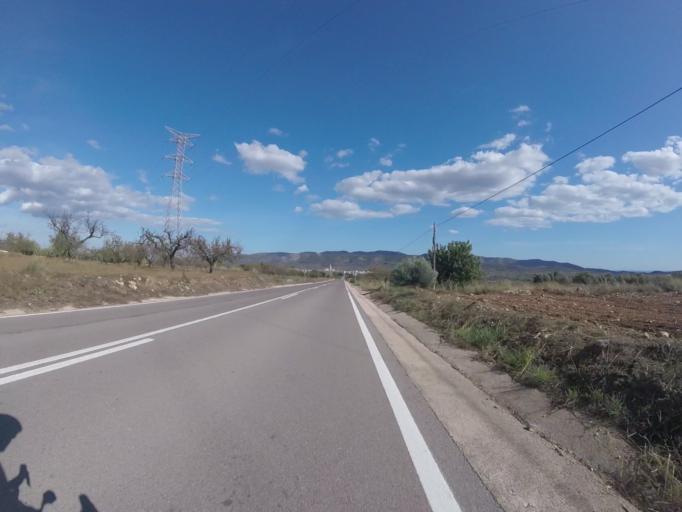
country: ES
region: Valencia
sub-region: Provincia de Castello
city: Alcala de Xivert
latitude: 40.3023
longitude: 0.1992
